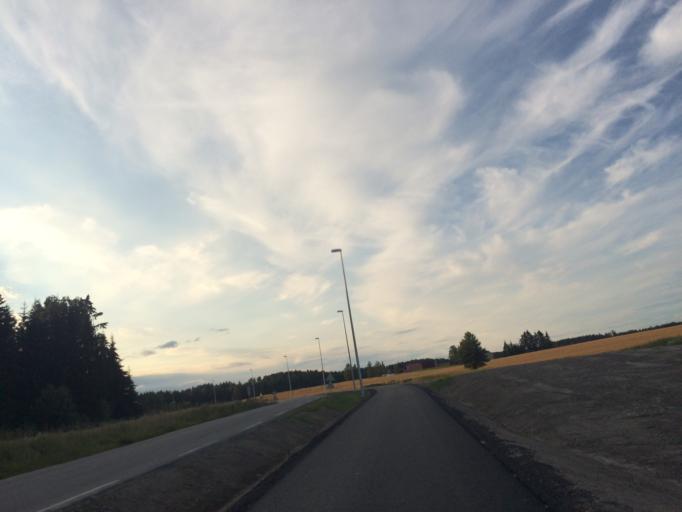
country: NO
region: Akershus
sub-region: Ski
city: Ski
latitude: 59.6947
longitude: 10.8592
